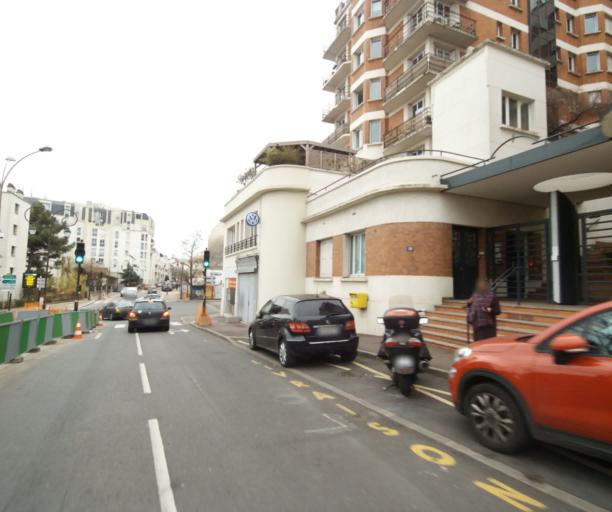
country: FR
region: Ile-de-France
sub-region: Departement des Hauts-de-Seine
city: Saint-Cloud
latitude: 48.8463
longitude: 2.2187
